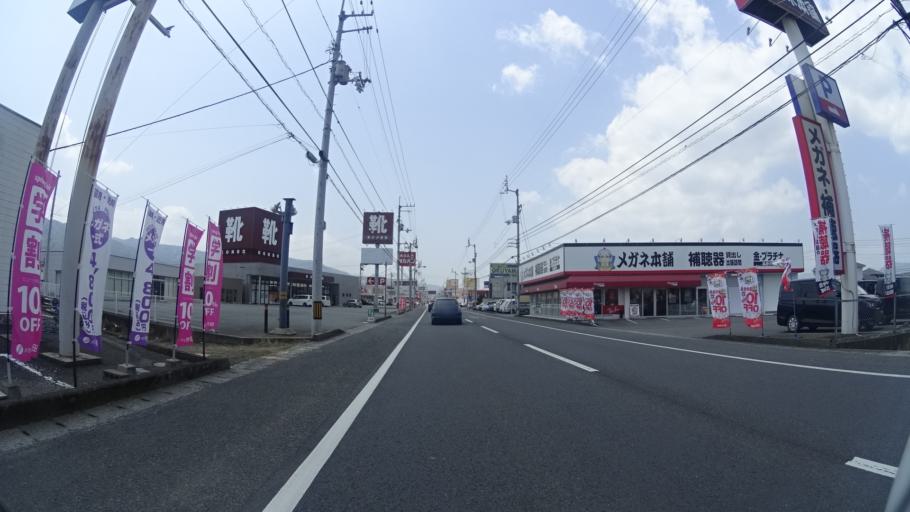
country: JP
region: Tokushima
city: Kamojimacho-jogejima
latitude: 34.0700
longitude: 134.3656
